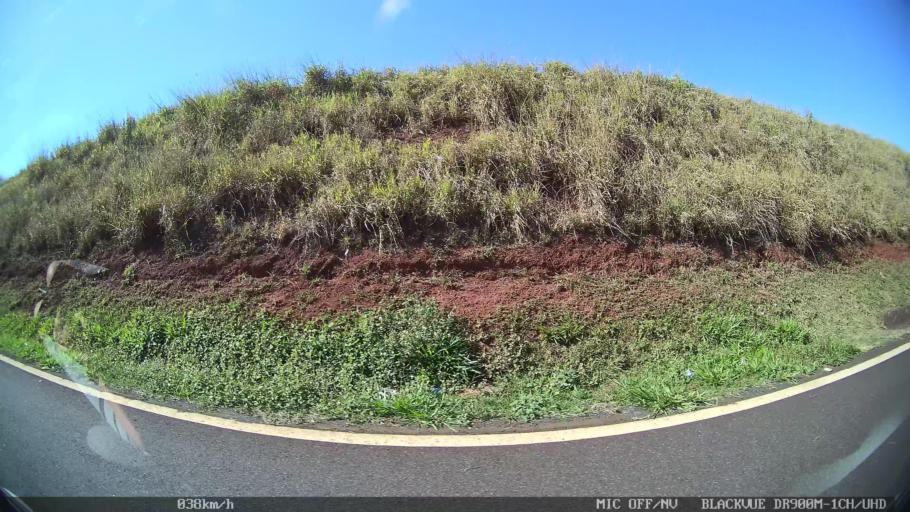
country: BR
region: Sao Paulo
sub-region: Franca
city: Franca
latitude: -20.6794
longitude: -47.4957
